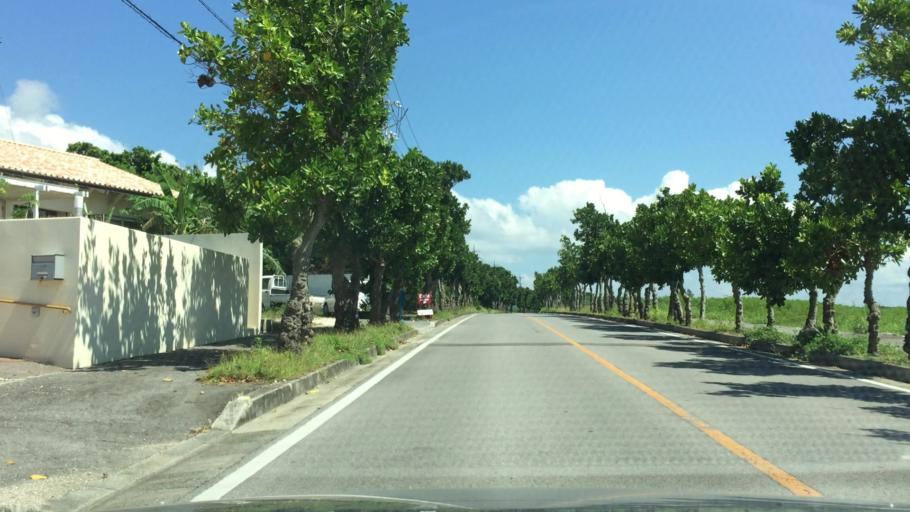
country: JP
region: Okinawa
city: Ishigaki
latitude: 24.3639
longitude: 124.2468
